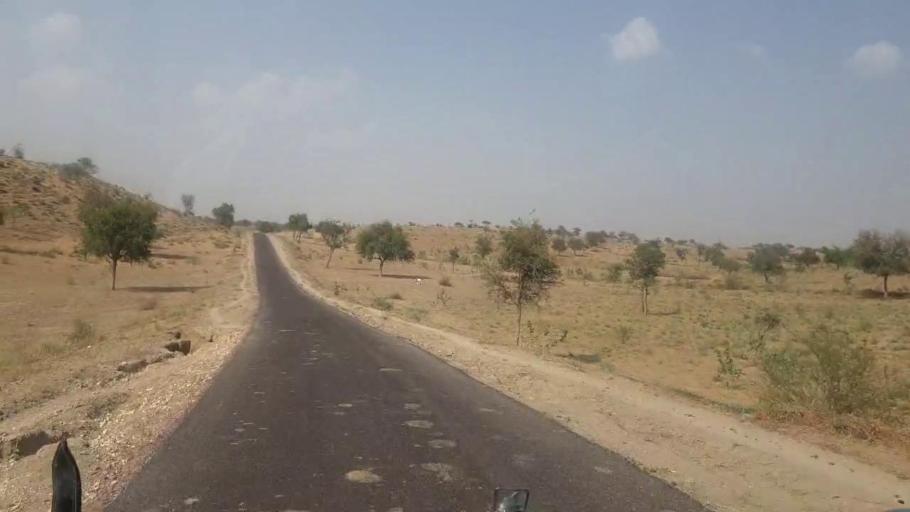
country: PK
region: Sindh
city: Islamkot
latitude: 25.1678
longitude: 70.2885
